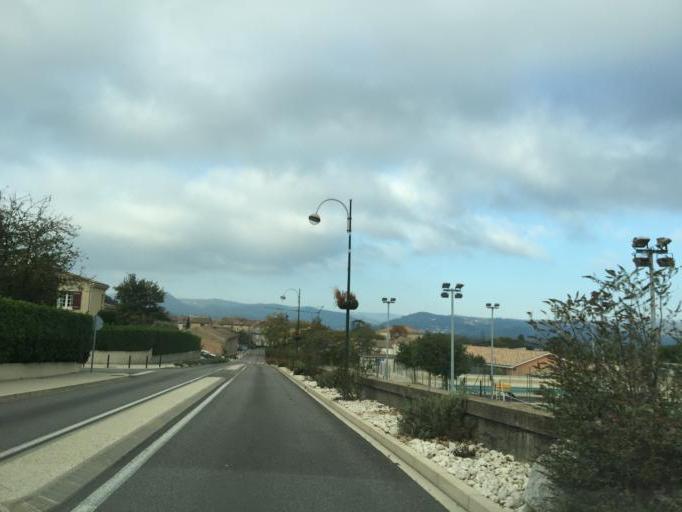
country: FR
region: Rhone-Alpes
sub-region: Departement de la Drome
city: Chateauneuf-du-Rhone
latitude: 44.4864
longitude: 4.7204
